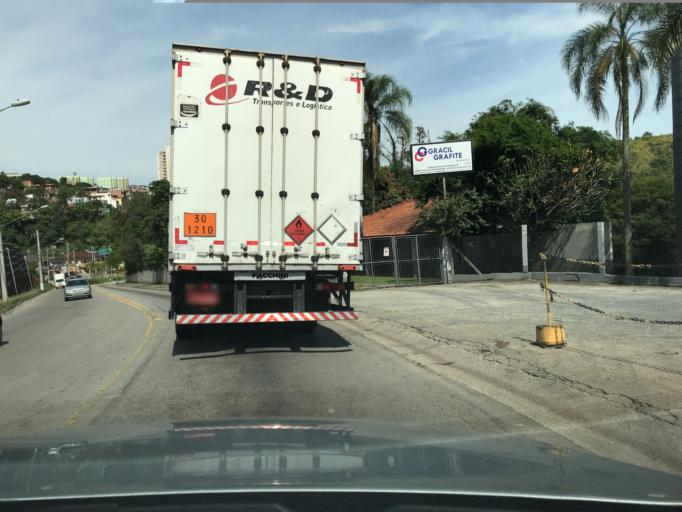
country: BR
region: Sao Paulo
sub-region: Cajamar
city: Cajamar
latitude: -23.4089
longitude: -46.8233
